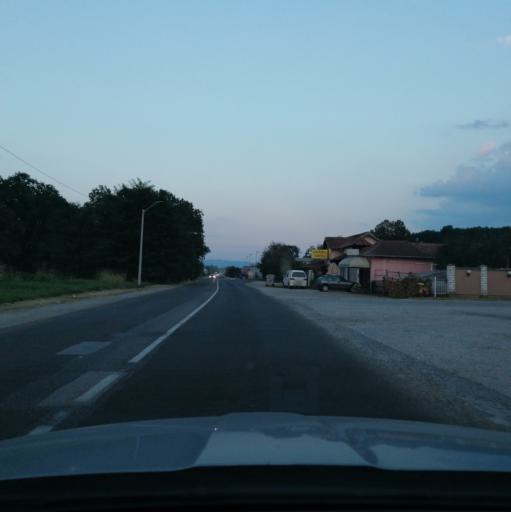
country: RS
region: Central Serbia
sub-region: Raski Okrug
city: Kraljevo
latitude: 43.7031
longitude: 20.7189
